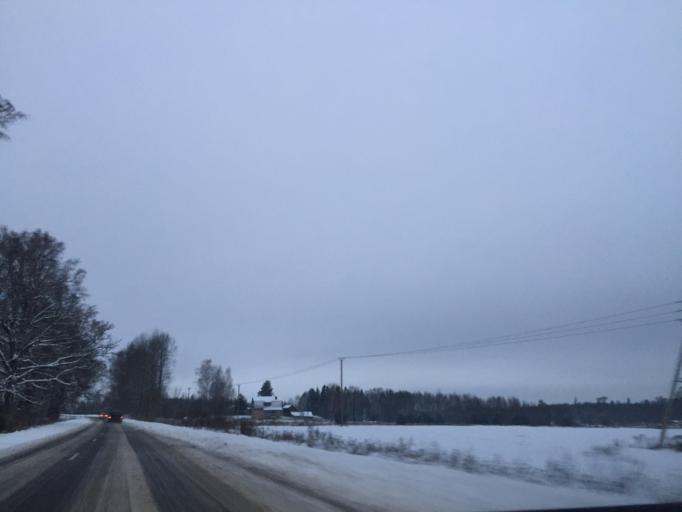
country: LV
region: Raunas
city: Rauna
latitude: 57.4351
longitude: 25.7075
